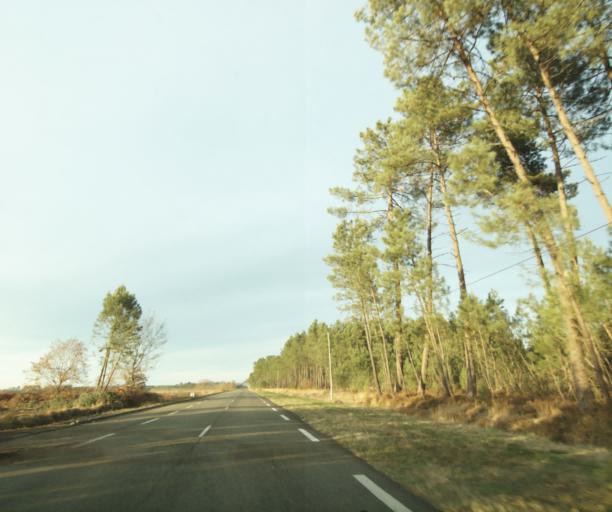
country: FR
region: Aquitaine
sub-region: Departement de la Gironde
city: Grignols
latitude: 44.1970
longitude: -0.1561
